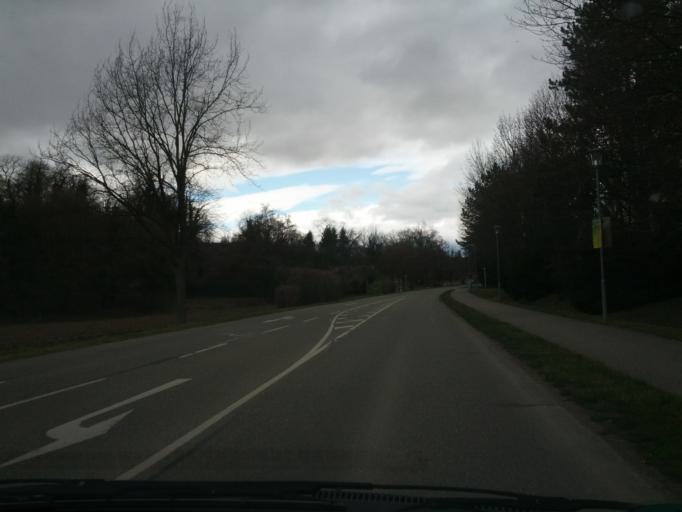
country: DE
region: Baden-Wuerttemberg
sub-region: Freiburg Region
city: Unterkrozingen
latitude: 47.9177
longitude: 7.6875
